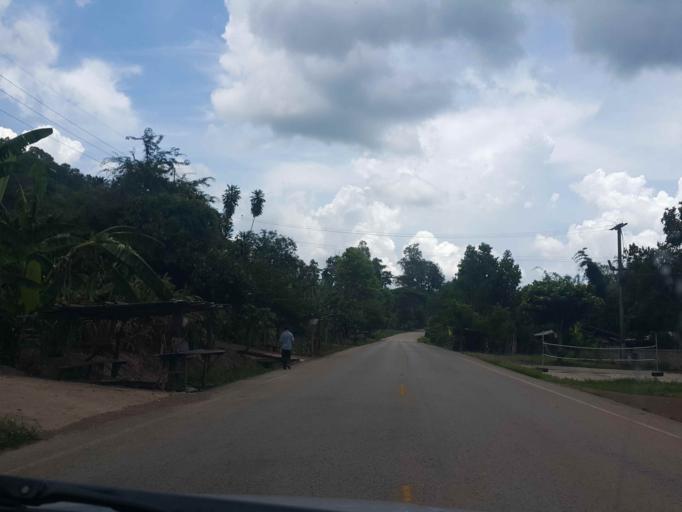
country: TH
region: Phayao
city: Chiang Muan
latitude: 18.9206
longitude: 100.1072
